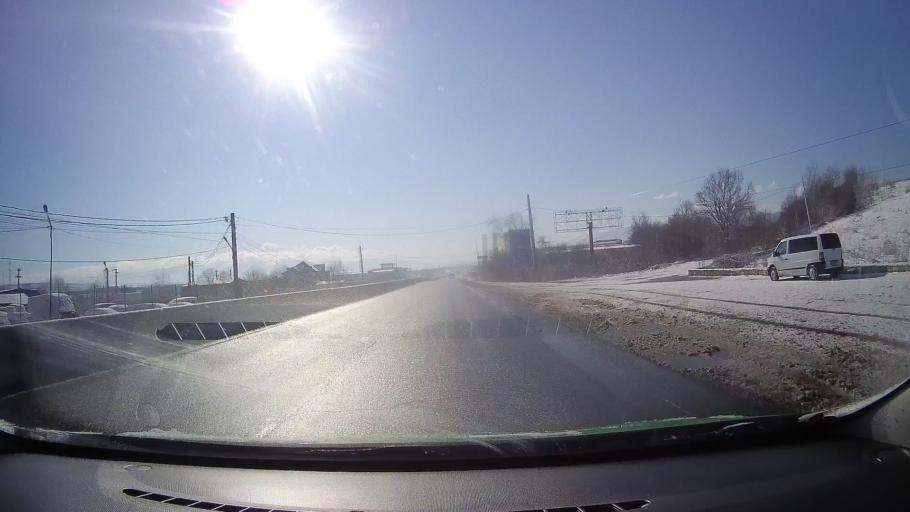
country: RO
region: Sibiu
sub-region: Comuna Selimbar
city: Selimbar
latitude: 45.7560
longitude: 24.1990
